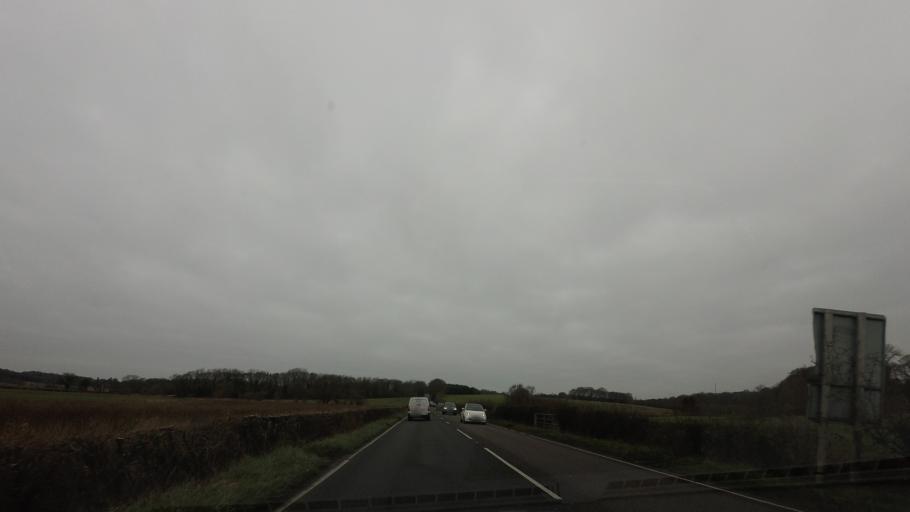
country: GB
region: England
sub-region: East Sussex
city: Battle
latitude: 50.9320
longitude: 0.5235
